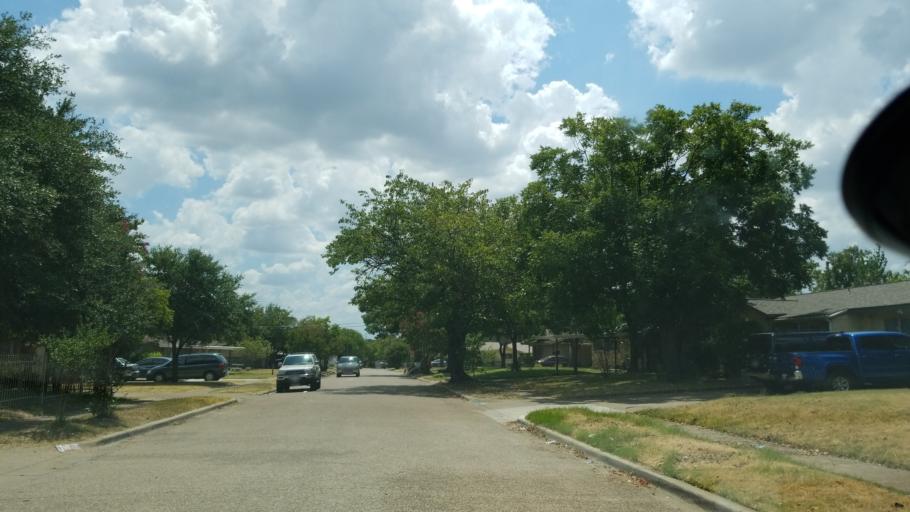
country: US
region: Texas
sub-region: Dallas County
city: Cockrell Hill
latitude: 32.7162
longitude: -96.8934
